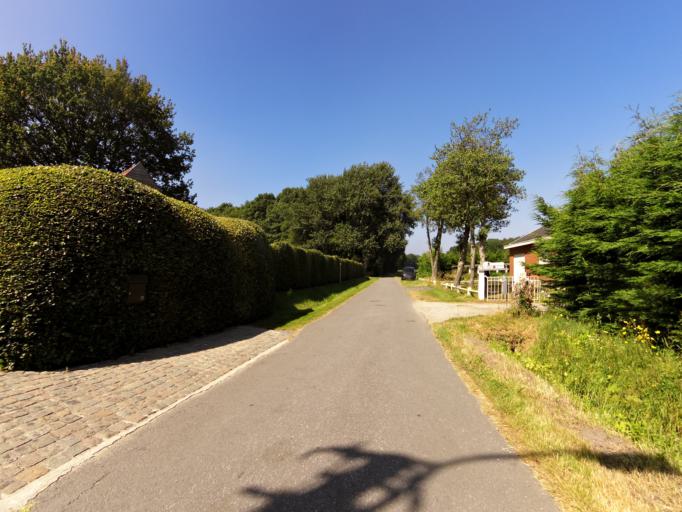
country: BE
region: Flanders
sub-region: Provincie West-Vlaanderen
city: Zedelgem
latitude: 51.1542
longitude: 3.1402
